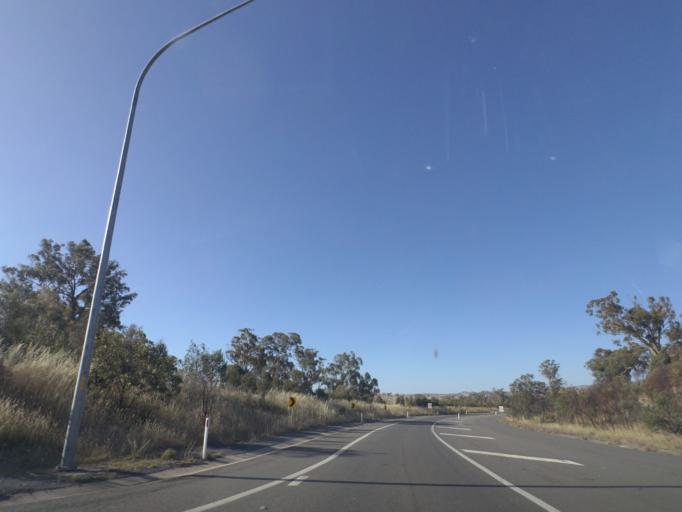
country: AU
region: New South Wales
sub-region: Wagga Wagga
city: Forest Hill
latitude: -35.2620
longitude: 147.7455
